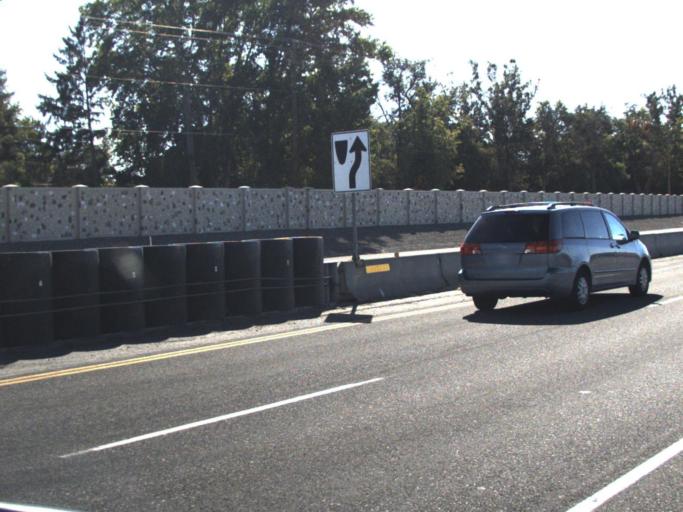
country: US
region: Washington
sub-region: Benton County
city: Richland
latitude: 46.2898
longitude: -119.3063
